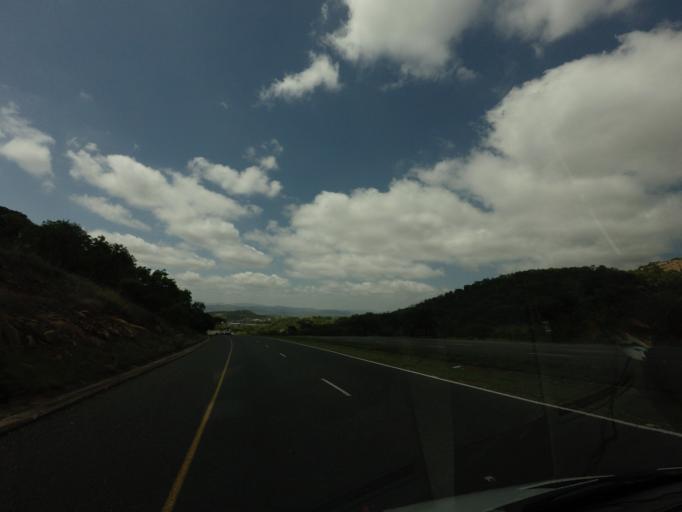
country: ZA
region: Mpumalanga
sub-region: Ehlanzeni District
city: White River
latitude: -25.3944
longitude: 30.9815
